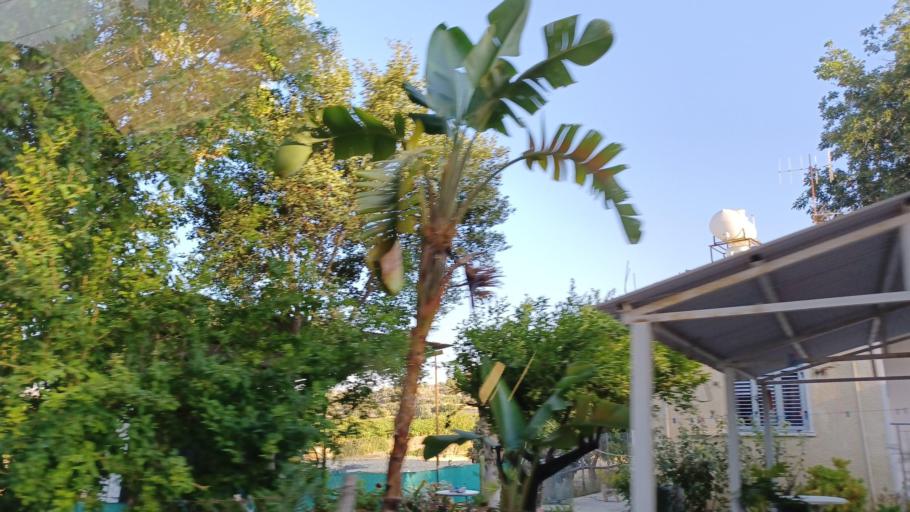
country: CY
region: Limassol
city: Pissouri
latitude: 34.7092
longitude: 32.6805
